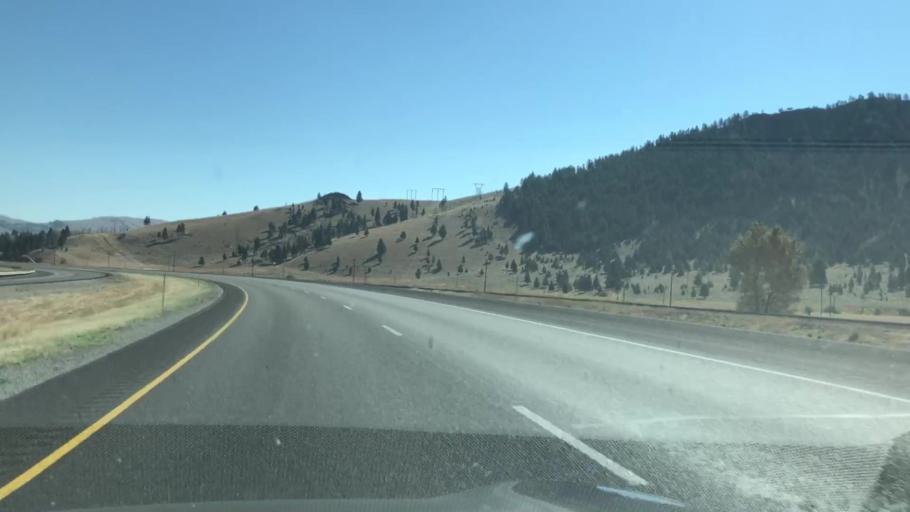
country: US
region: Montana
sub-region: Missoula County
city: Clinton
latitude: 46.6973
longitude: -113.3567
